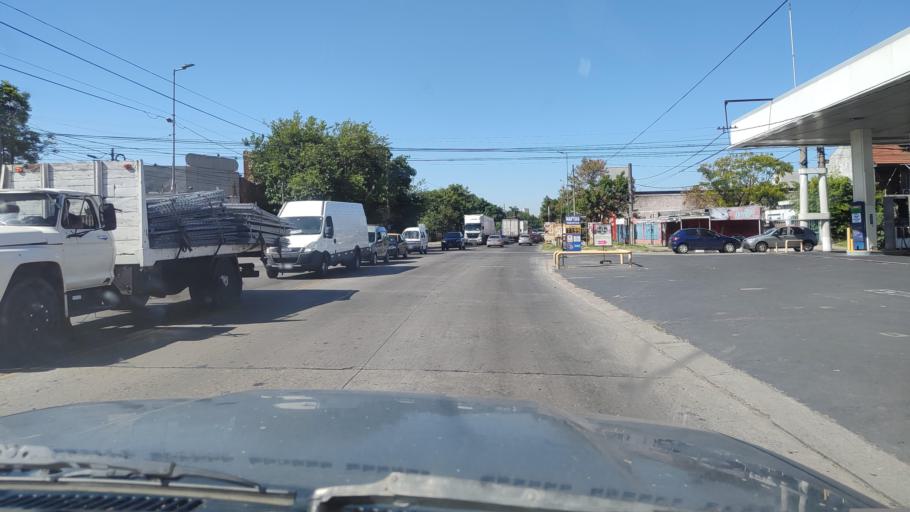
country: AR
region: Buenos Aires
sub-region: Partido de Moron
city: Moron
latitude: -34.6431
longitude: -58.6254
